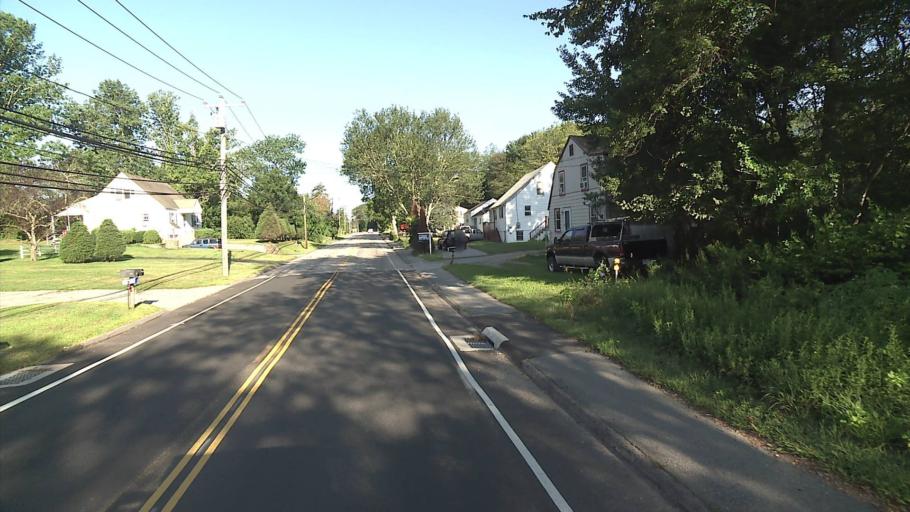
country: US
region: Connecticut
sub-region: New London County
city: Central Waterford
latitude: 41.3485
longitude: -72.1465
